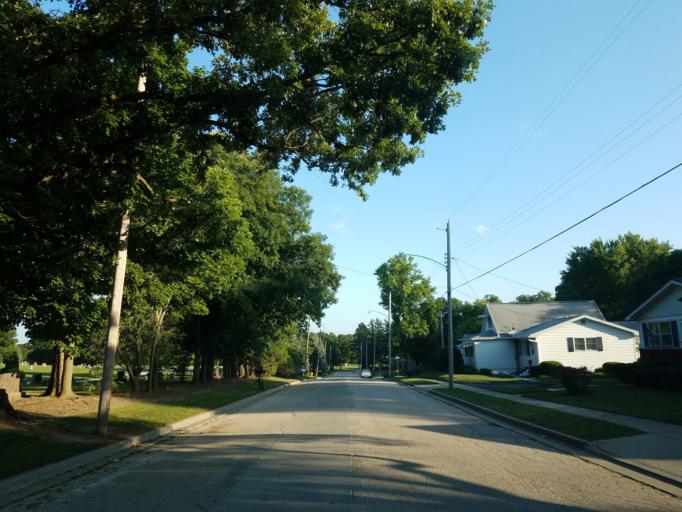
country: US
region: Illinois
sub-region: McLean County
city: Bloomington
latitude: 40.4682
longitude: -89.0098
